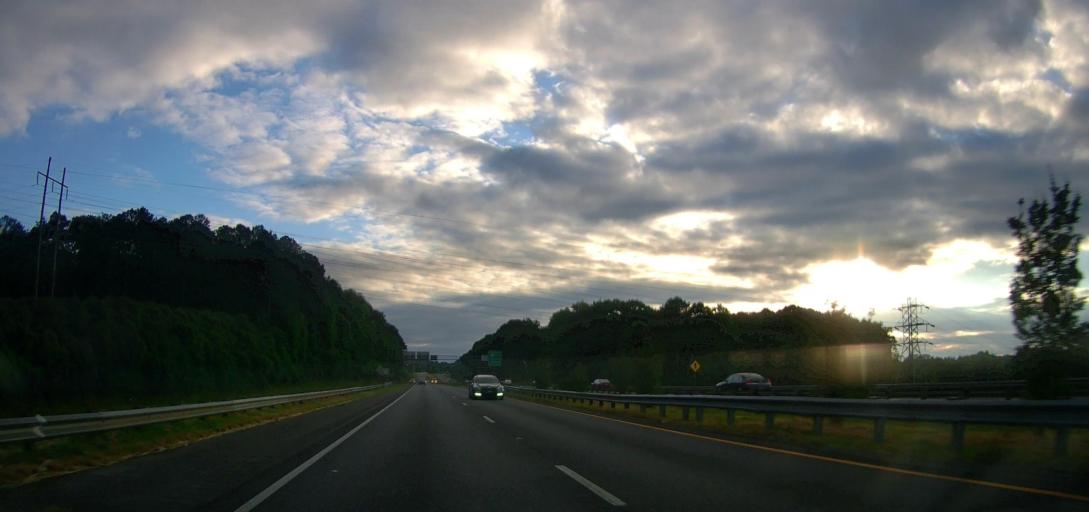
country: US
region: Georgia
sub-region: Clarke County
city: Athens
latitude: 33.9738
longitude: -83.3931
